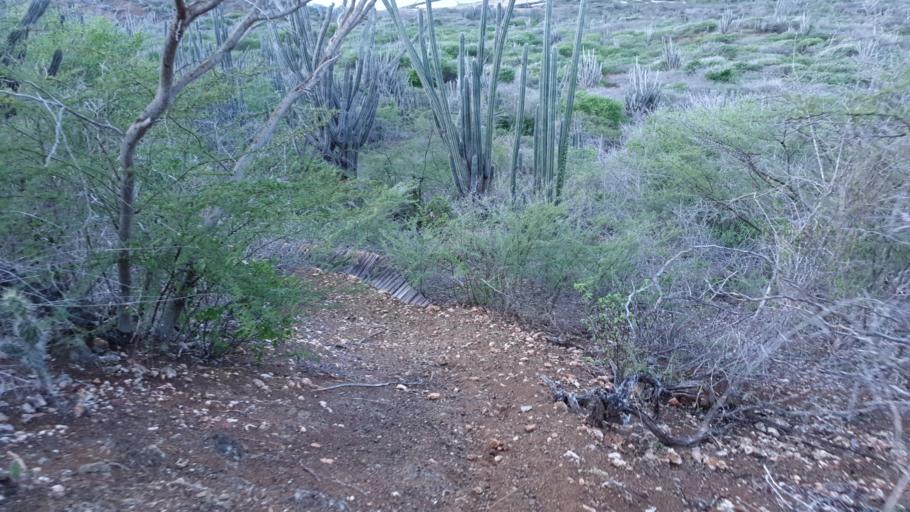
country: CW
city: Newport
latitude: 12.1318
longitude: -68.8156
